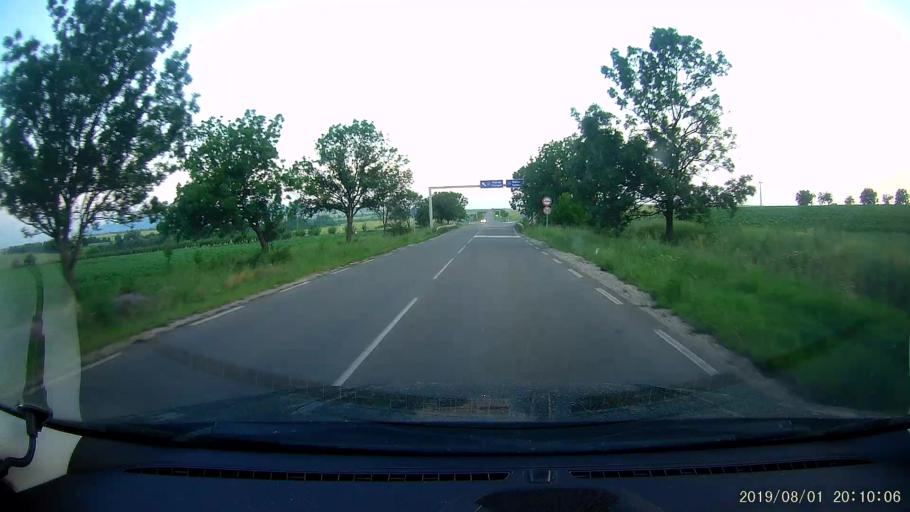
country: BG
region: Yambol
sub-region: Obshtina Yambol
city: Yambol
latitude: 42.4870
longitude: 26.5965
